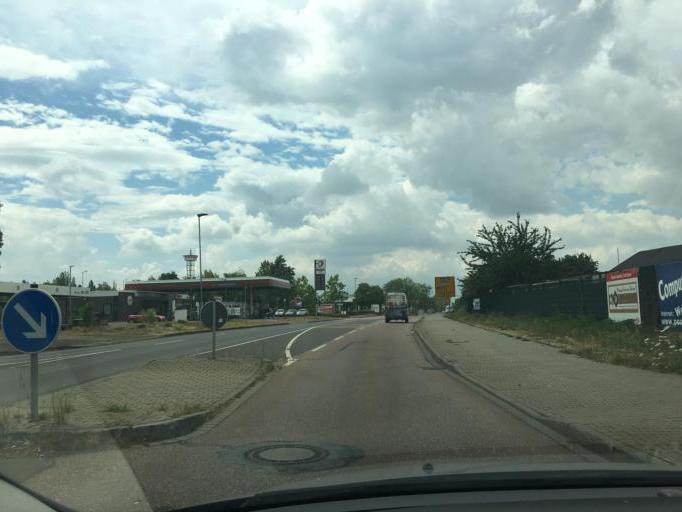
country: DE
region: Saxony-Anhalt
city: Merseburg
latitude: 51.3722
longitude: 11.9843
